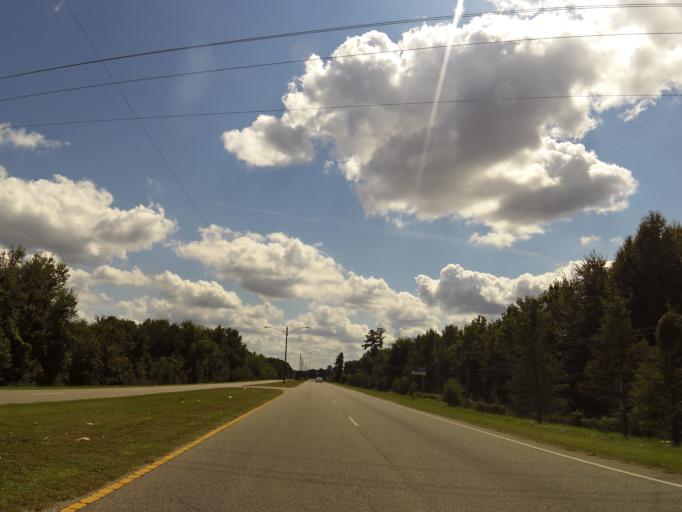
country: US
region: Alabama
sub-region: Dallas County
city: Selmont-West Selmont
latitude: 32.3809
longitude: -87.0104
